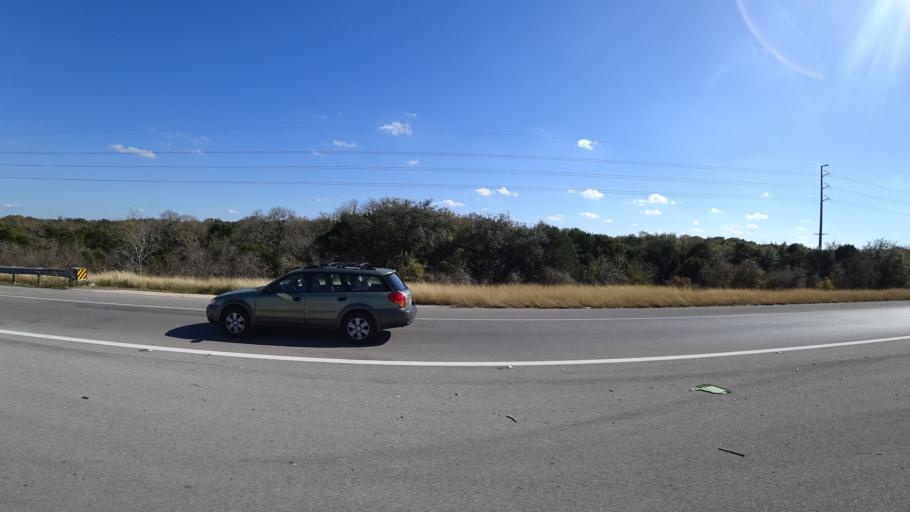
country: US
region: Texas
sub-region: Travis County
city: Shady Hollow
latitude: 30.2109
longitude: -97.8583
